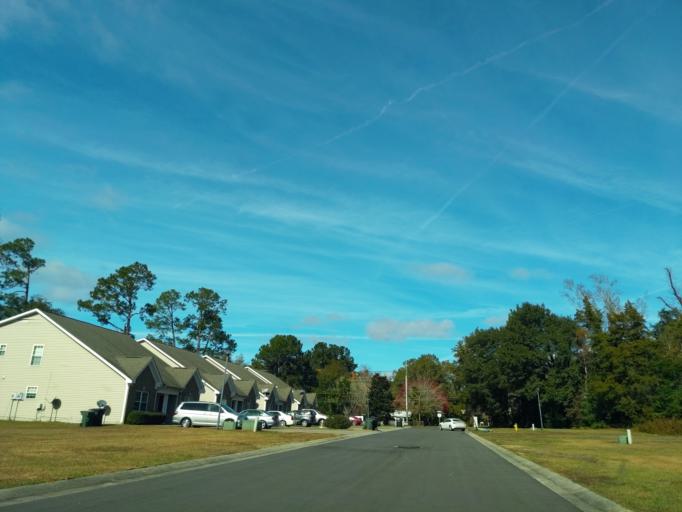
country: US
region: Florida
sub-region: Leon County
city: Tallahassee
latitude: 30.4727
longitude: -84.3421
